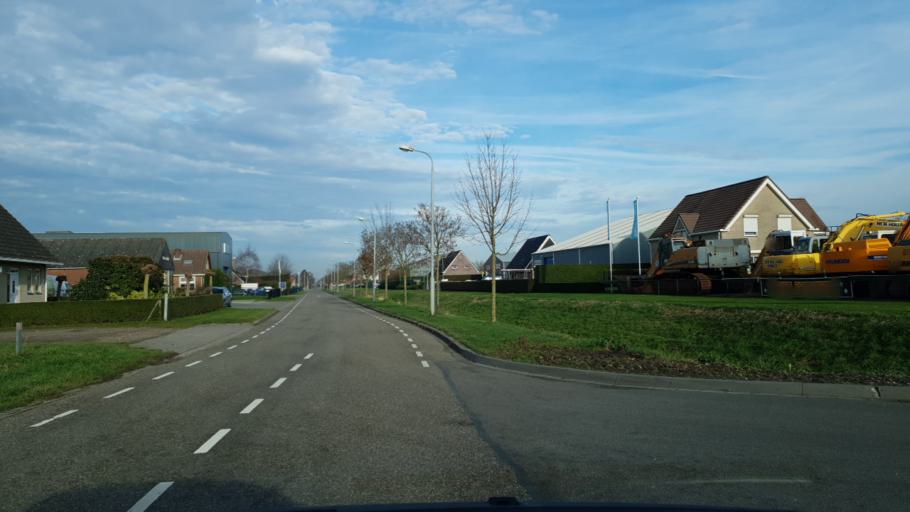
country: NL
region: Zeeland
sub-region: Gemeente Reimerswaal
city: Yerseke
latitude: 51.4216
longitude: 4.1093
